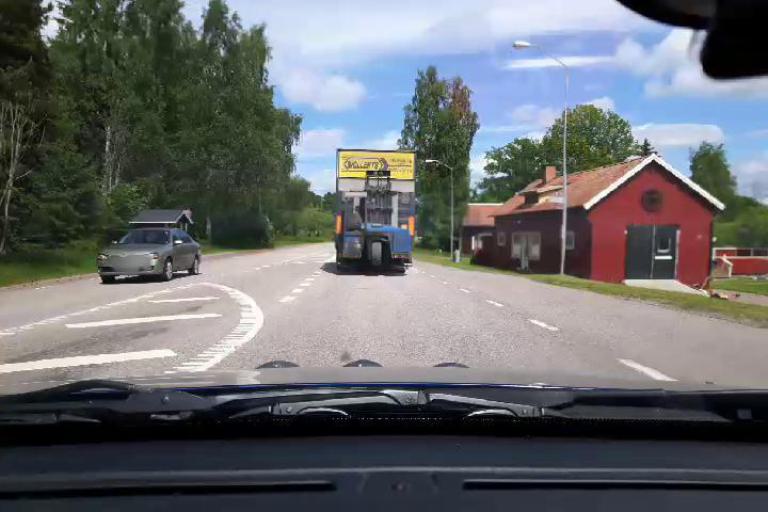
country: SE
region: Uppsala
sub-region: Osthammars Kommun
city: Bjorklinge
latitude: 60.0869
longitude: 17.5514
